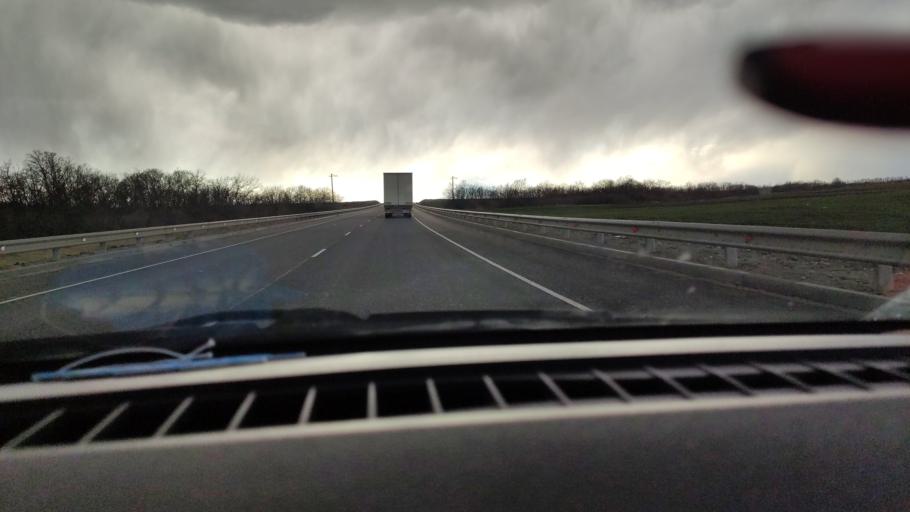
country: RU
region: Saratov
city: Yelshanka
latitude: 51.8309
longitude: 46.4450
